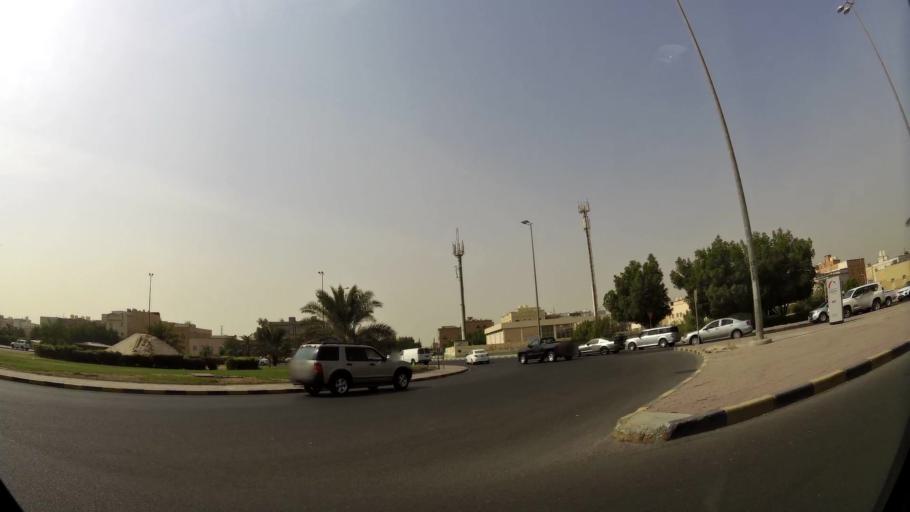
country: KW
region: Al Asimah
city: Ar Rabiyah
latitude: 29.2850
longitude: 47.9066
